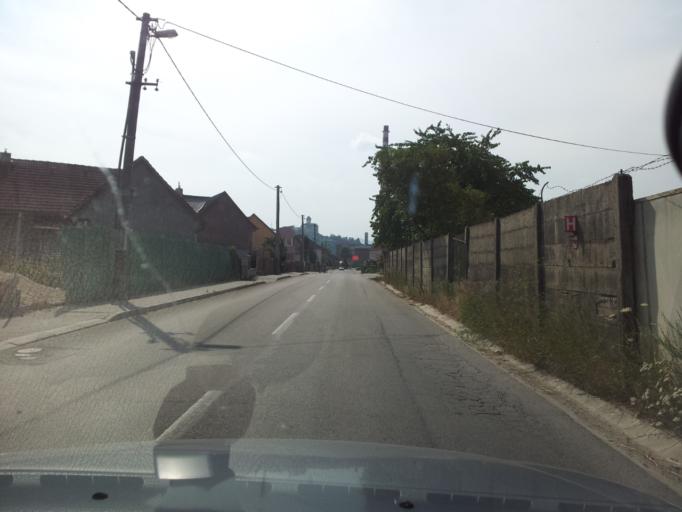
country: SK
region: Trenciansky
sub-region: Okres Trencin
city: Trencin
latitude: 48.8937
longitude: 18.0666
